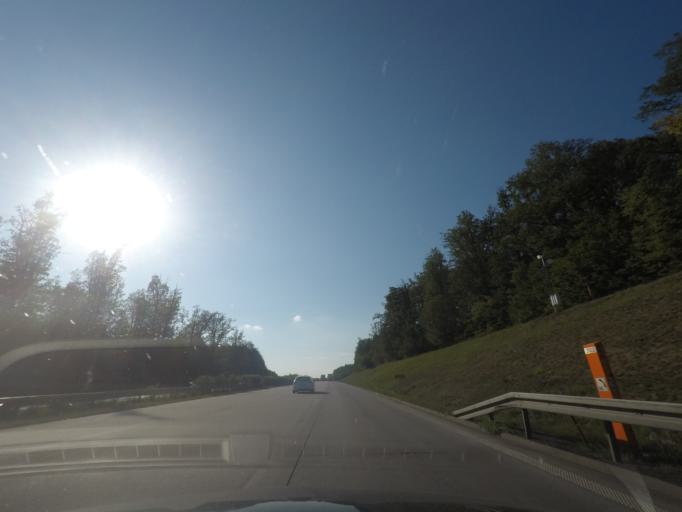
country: CZ
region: Olomoucky
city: Dolni Ujezd
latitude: 49.5568
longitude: 17.5219
